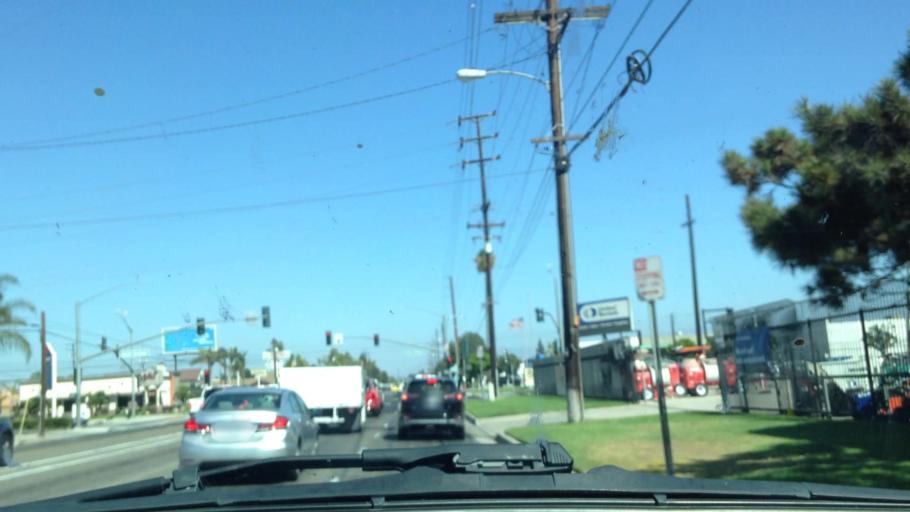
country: US
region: California
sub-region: Orange County
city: Placentia
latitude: 33.8596
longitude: -117.8904
